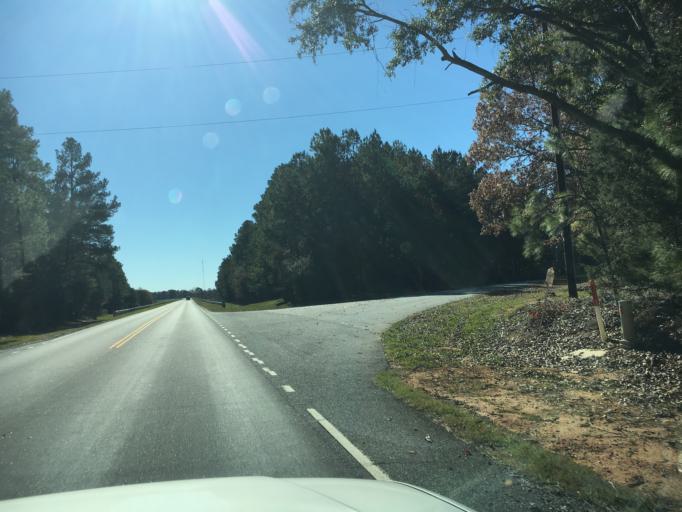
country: US
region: Georgia
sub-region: Hart County
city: Hartwell
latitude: 34.3763
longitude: -82.8123
